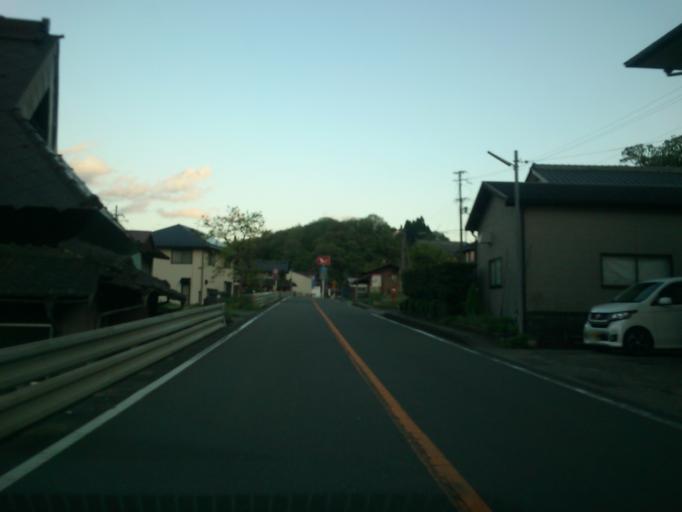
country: JP
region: Kyoto
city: Ayabe
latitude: 35.2114
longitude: 135.4258
